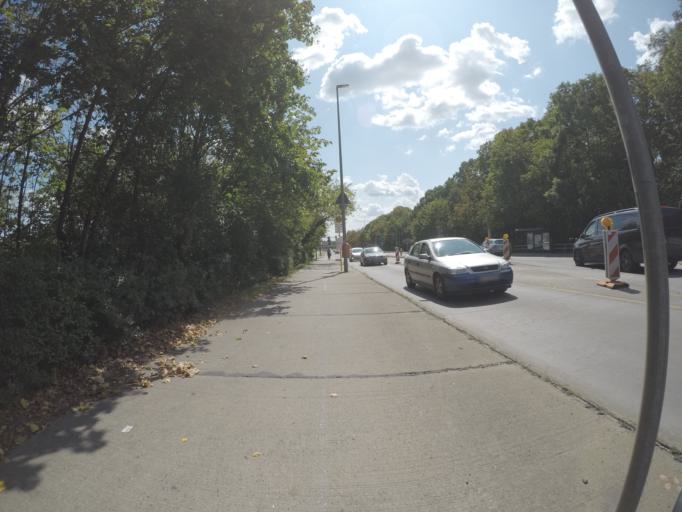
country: DE
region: Berlin
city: Biesdorf
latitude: 52.5121
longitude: 13.5625
